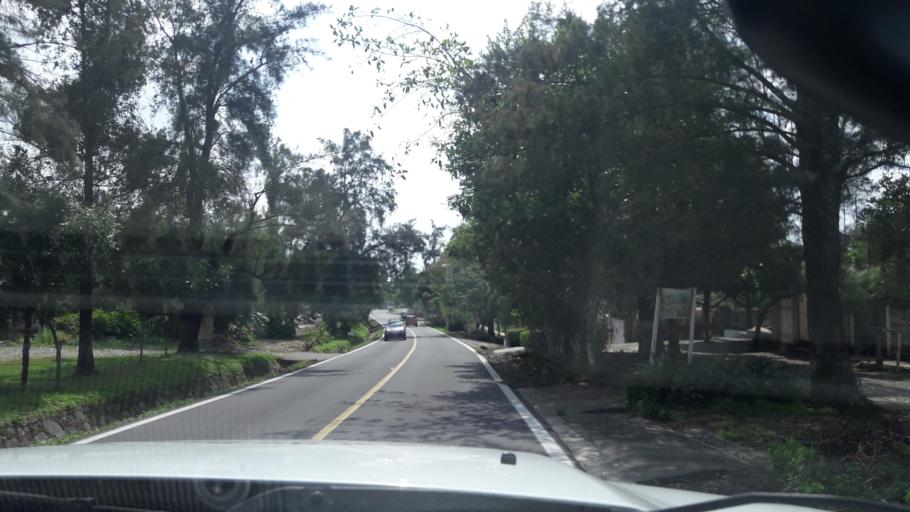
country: MX
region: Colima
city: Suchitlan
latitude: 19.3936
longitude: -103.7051
